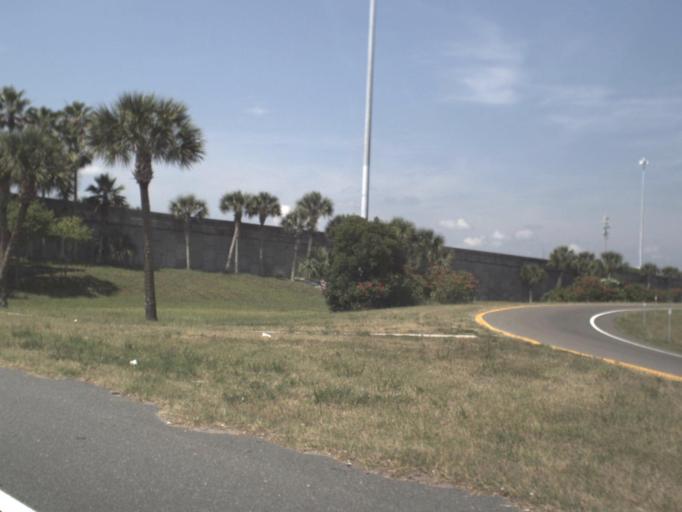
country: US
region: Florida
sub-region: Saint Johns County
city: Ponte Vedra Beach
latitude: 30.2567
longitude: -81.3883
